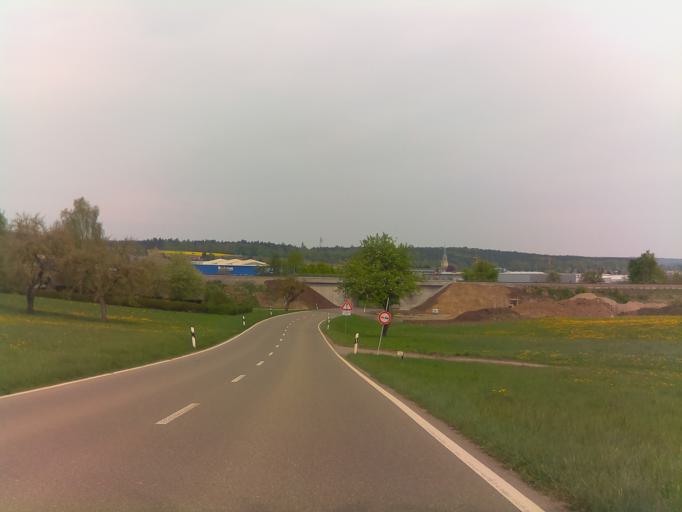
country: DE
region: Baden-Wuerttemberg
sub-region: Freiburg Region
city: Deisslingen
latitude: 48.0990
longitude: 8.5964
